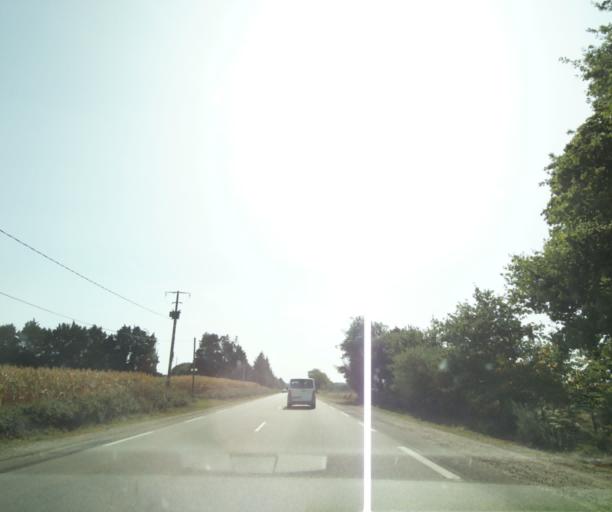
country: FR
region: Brittany
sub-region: Departement du Morbihan
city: Riantec
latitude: 47.7459
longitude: -3.2981
